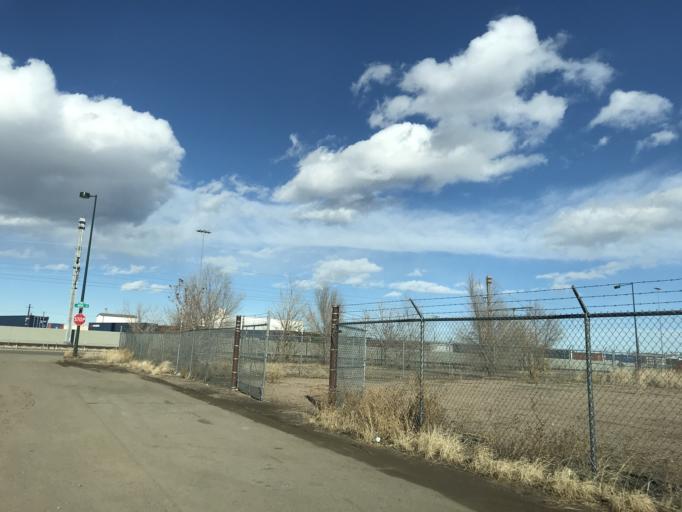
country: US
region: Colorado
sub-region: Denver County
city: Denver
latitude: 39.7724
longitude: -104.9635
